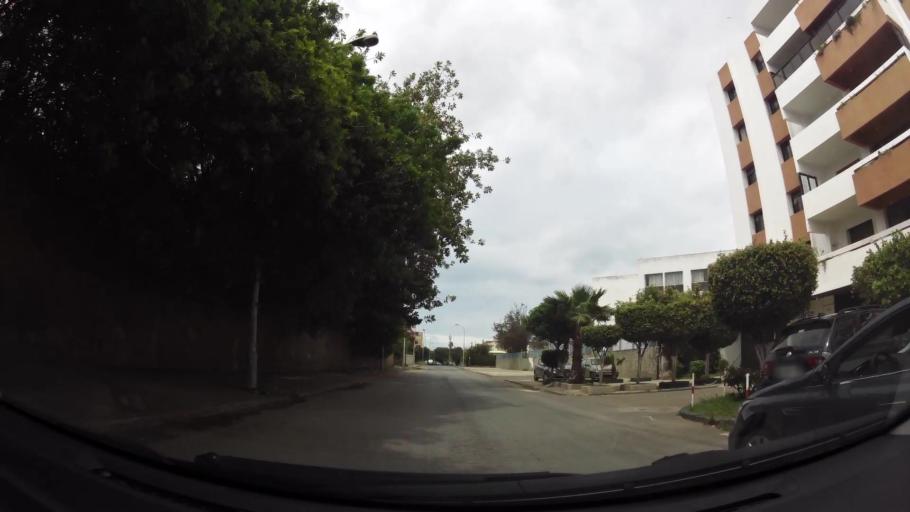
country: MA
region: Grand Casablanca
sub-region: Casablanca
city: Casablanca
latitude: 33.5744
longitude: -7.6524
